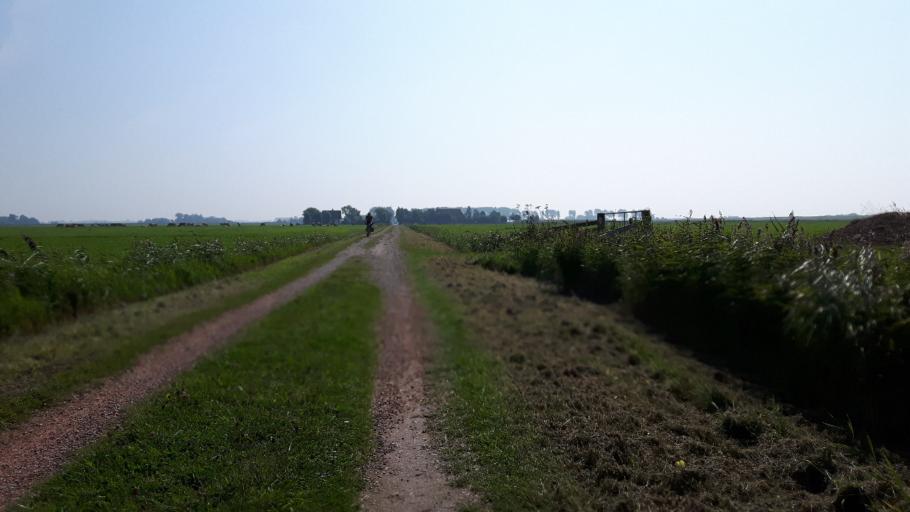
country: NL
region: Friesland
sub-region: Sudwest Fryslan
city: Workum
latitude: 52.9582
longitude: 5.4193
